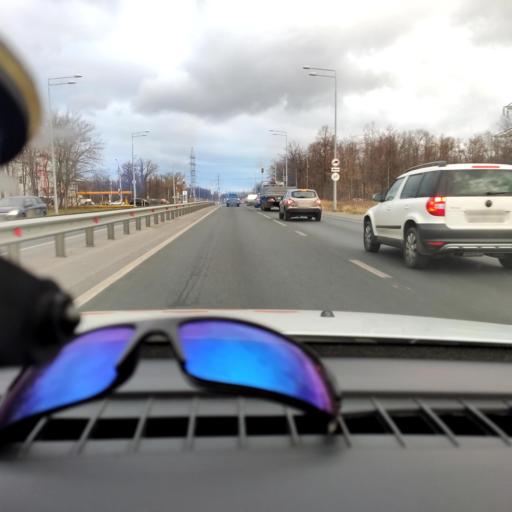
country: RU
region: Samara
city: Novosemeykino
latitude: 53.3456
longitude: 50.2340
